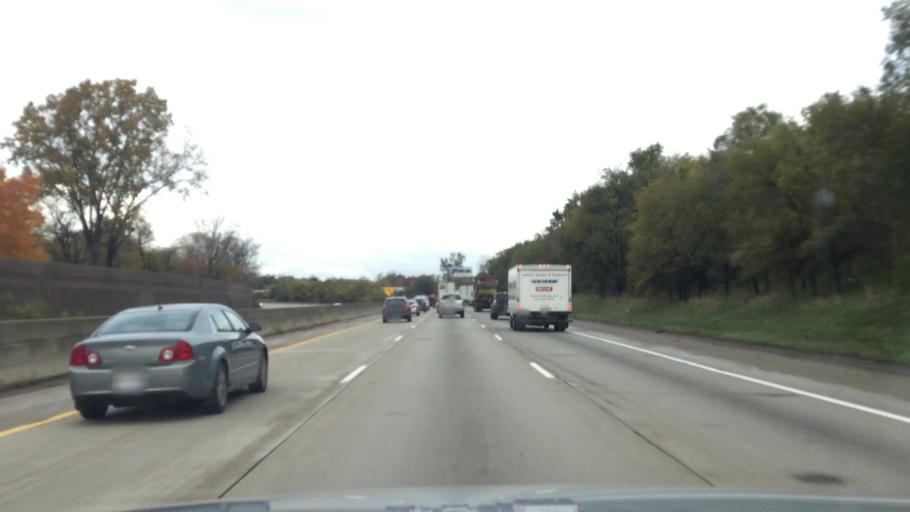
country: US
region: Michigan
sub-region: Washtenaw County
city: Ypsilanti
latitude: 42.2290
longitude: -83.5742
